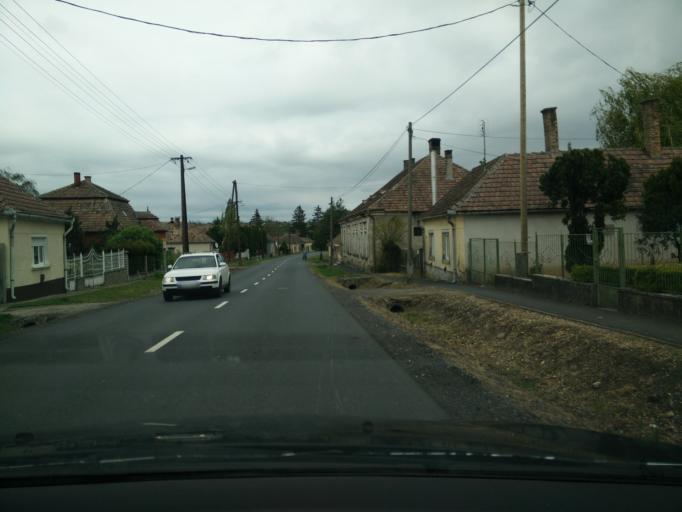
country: HU
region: Zala
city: Turje
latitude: 46.9863
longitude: 17.0967
